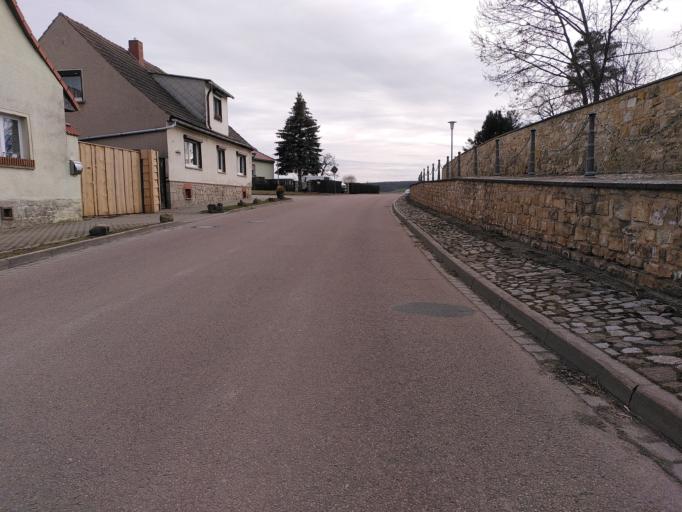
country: DE
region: Saxony-Anhalt
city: Ballenstedt
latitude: 51.7596
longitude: 11.2422
